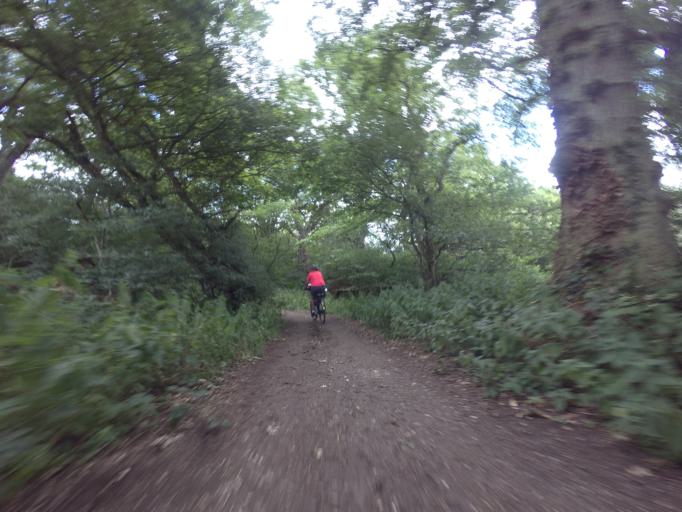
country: GB
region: England
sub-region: East Sussex
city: Hailsham
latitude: 50.8364
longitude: 0.2244
